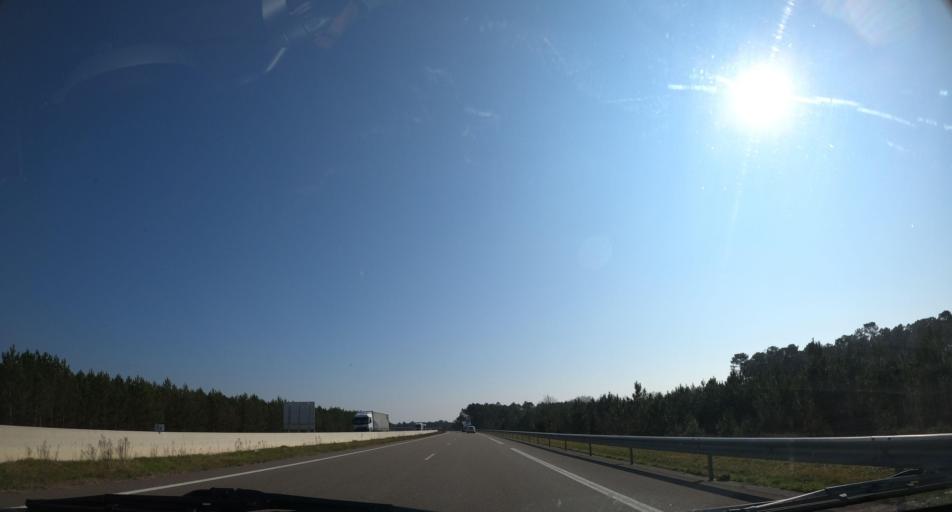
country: FR
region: Aquitaine
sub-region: Departement des Landes
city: Saint-Geours-de-Maremne
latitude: 43.6951
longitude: -1.2155
